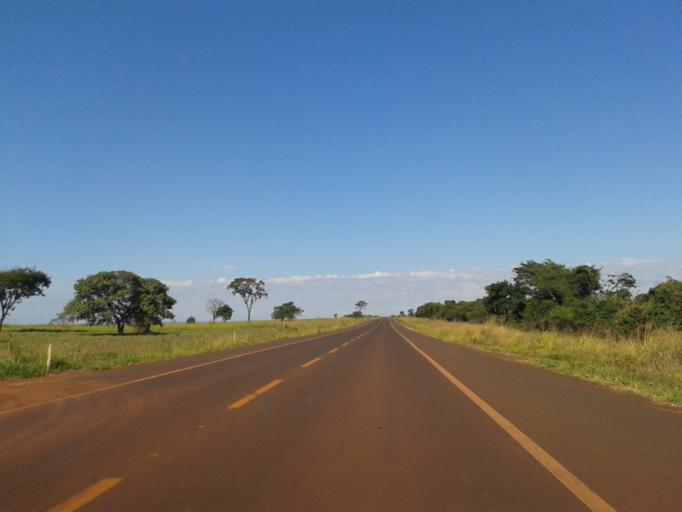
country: BR
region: Minas Gerais
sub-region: Ituiutaba
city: Ituiutaba
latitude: -19.0745
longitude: -49.5039
